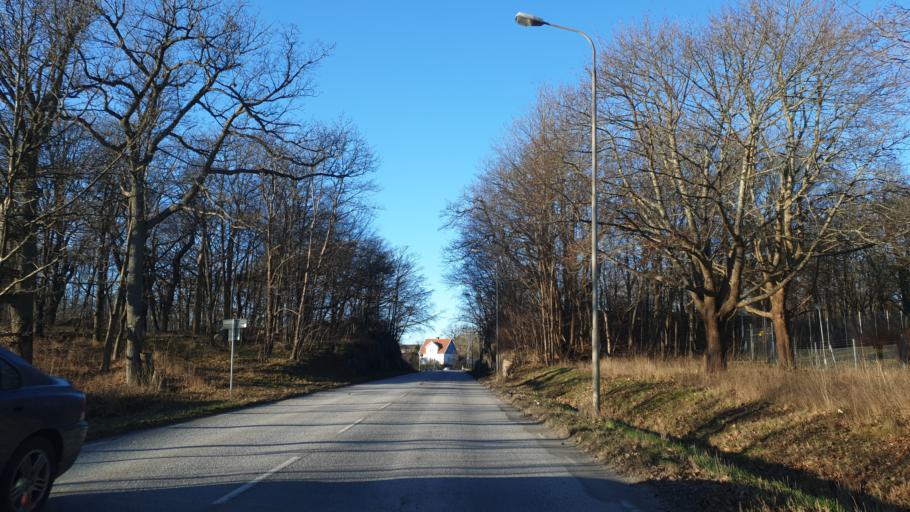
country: SE
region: Blekinge
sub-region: Karlskrona Kommun
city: Rodeby
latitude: 56.2040
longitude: 15.6350
